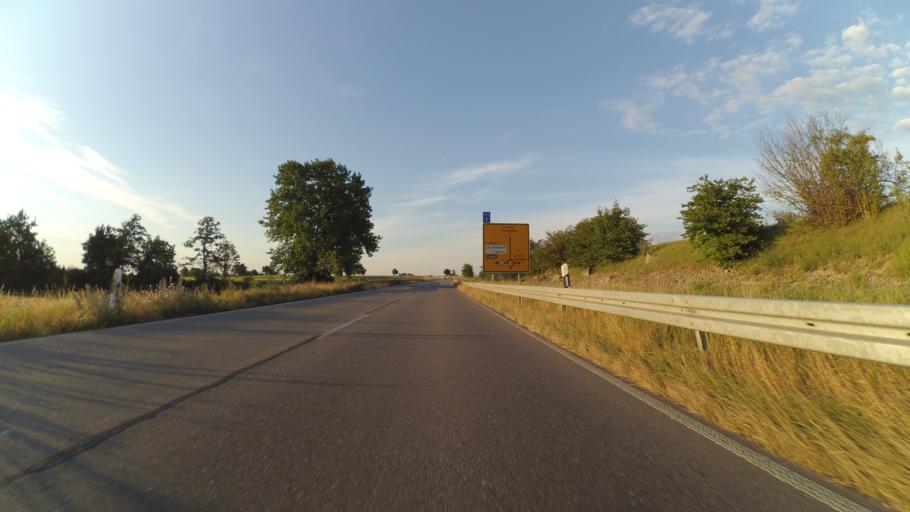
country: DE
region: Baden-Wuerttemberg
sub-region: Freiburg Region
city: Eschbach
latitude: 47.8861
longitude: 7.6666
